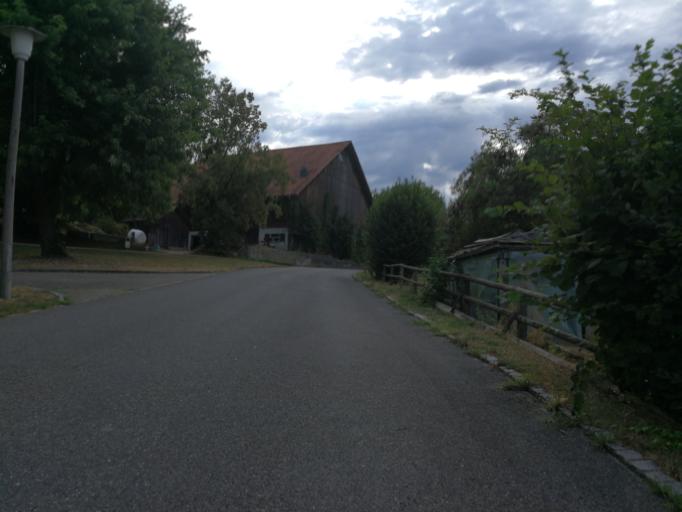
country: CH
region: Zurich
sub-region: Bezirk Hinwil
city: Gossau
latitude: 47.3301
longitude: 8.7580
